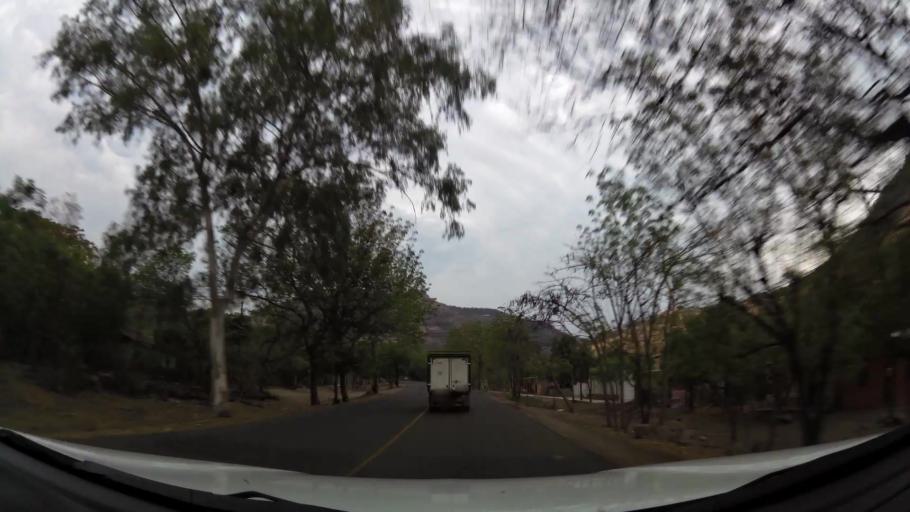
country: NI
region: Leon
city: Santa Rosa del Penon
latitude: 12.9376
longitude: -86.2062
